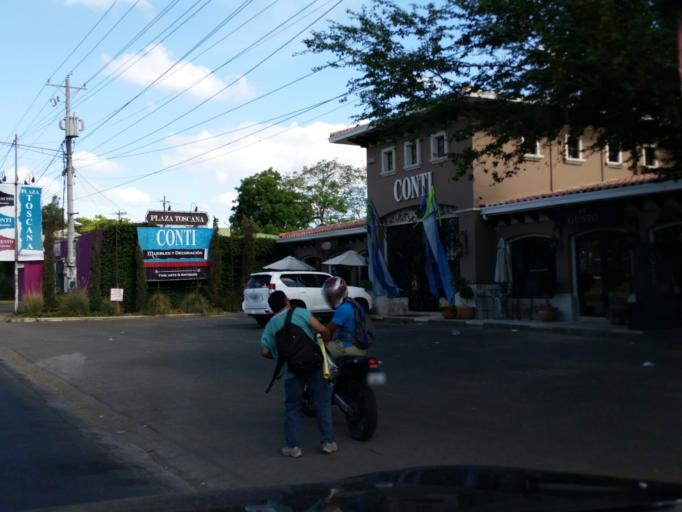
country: NI
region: Managua
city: Managua
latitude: 12.1027
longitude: -86.2610
